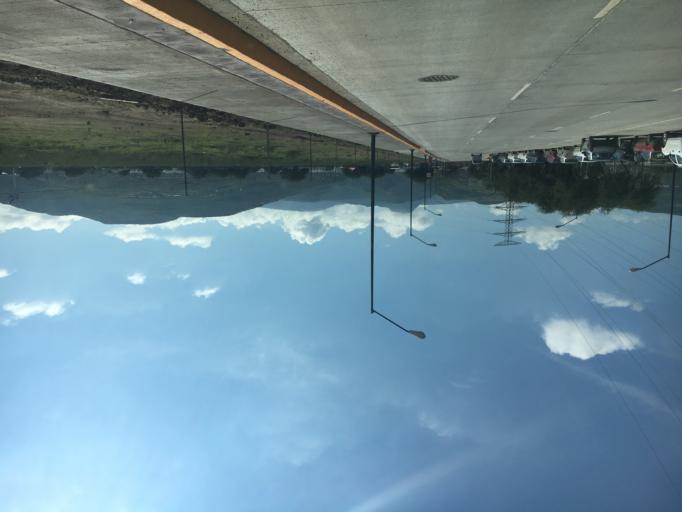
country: MX
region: Guanajuato
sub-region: Leon
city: Medina
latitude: 21.1348
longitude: -101.6227
